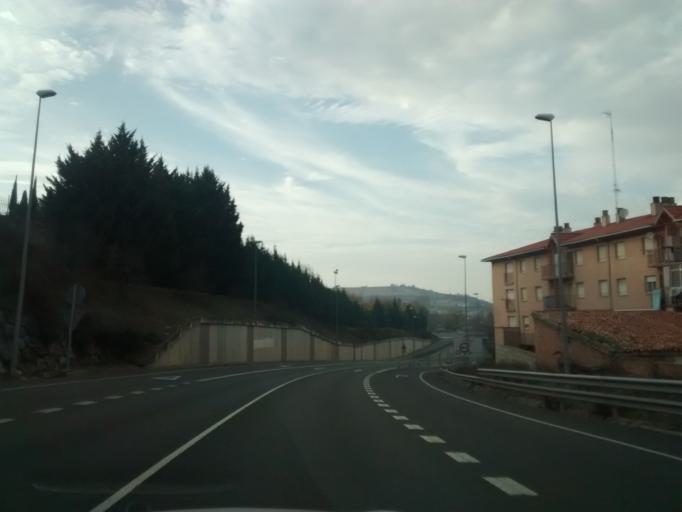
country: ES
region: La Rioja
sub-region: Provincia de La Rioja
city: Cenicero
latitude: 42.4804
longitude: -2.6466
